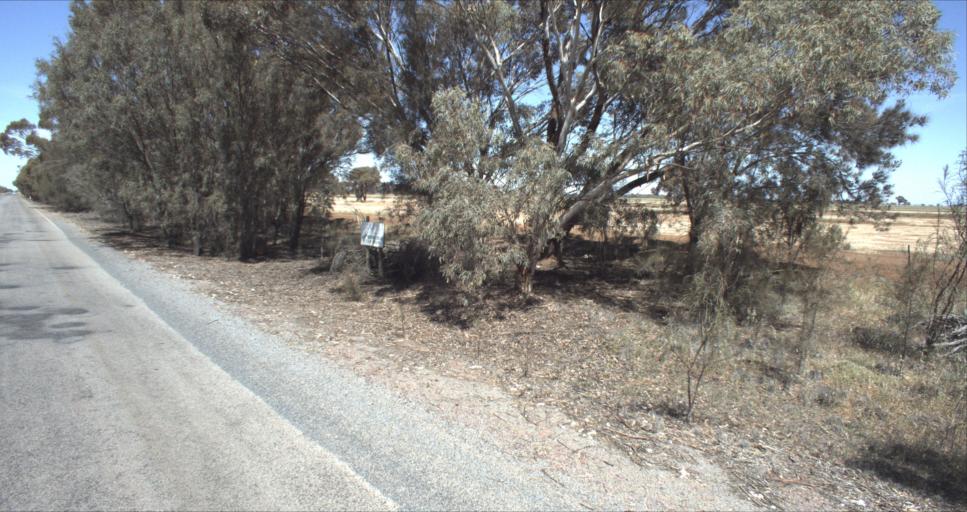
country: AU
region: New South Wales
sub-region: Leeton
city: Leeton
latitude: -34.4683
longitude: 146.2928
